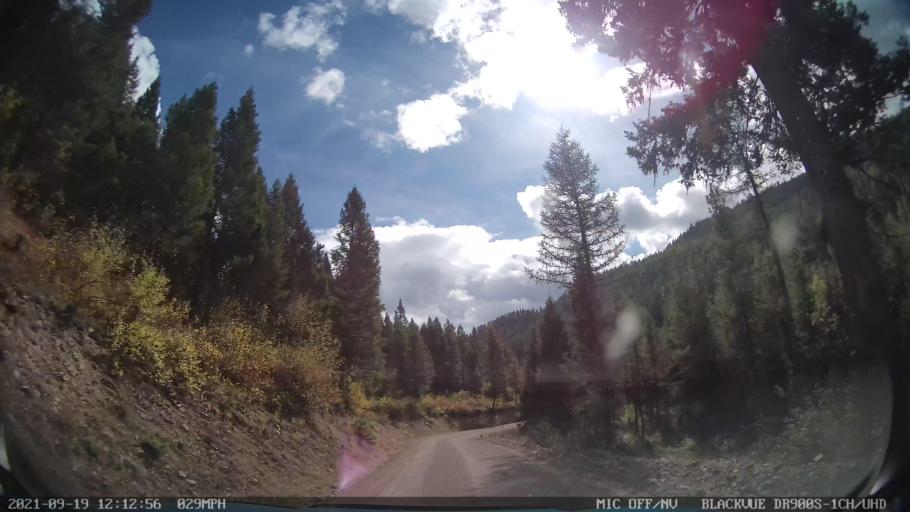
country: US
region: Montana
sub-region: Missoula County
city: Seeley Lake
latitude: 47.1698
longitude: -113.3610
